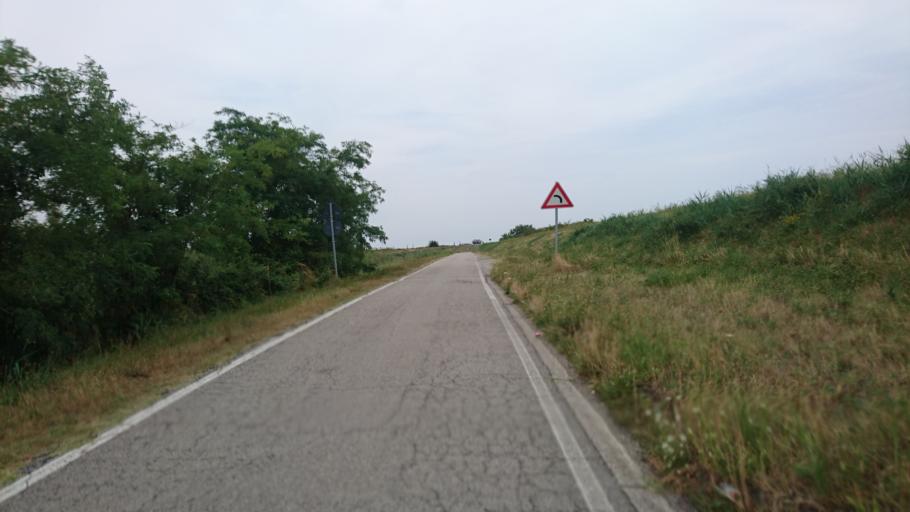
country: IT
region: Veneto
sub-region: Provincia di Rovigo
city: Rosolina
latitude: 45.0738
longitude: 12.3019
